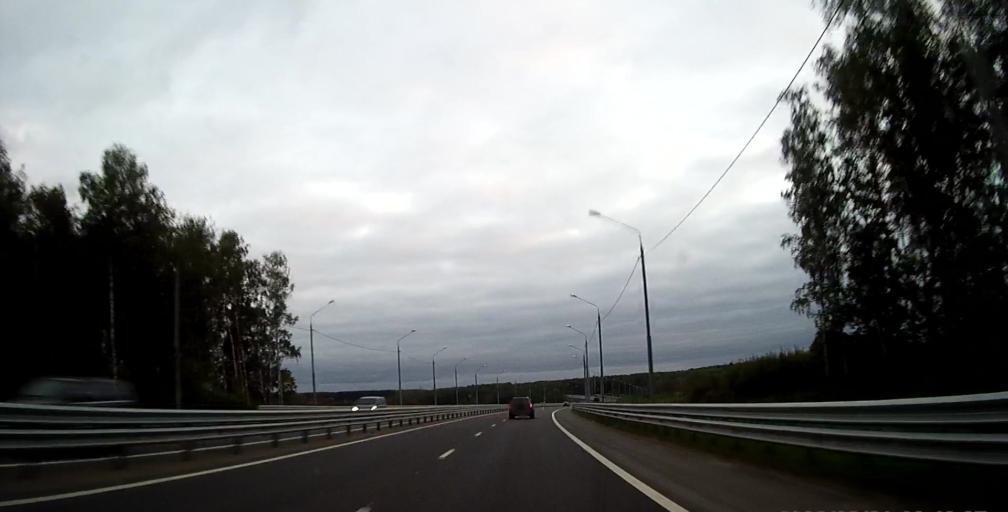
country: RU
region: Moskovskaya
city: Dubrovitsy
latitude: 55.4126
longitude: 37.5002
